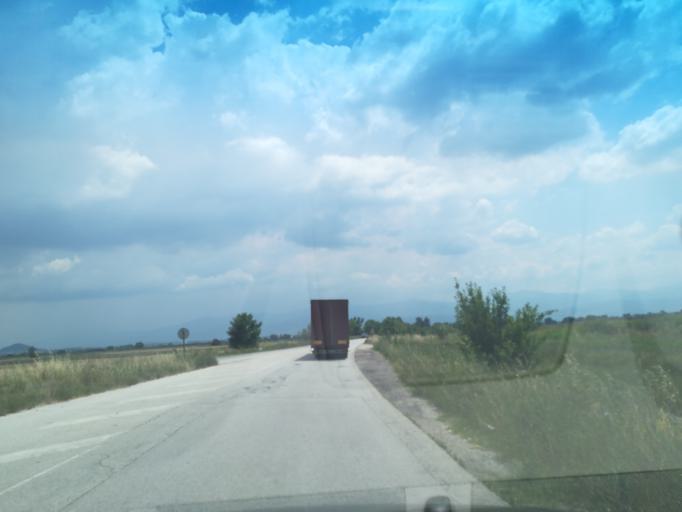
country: BG
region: Plovdiv
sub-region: Obshtina Plovdiv
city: Plovdiv
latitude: 42.1856
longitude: 24.6763
